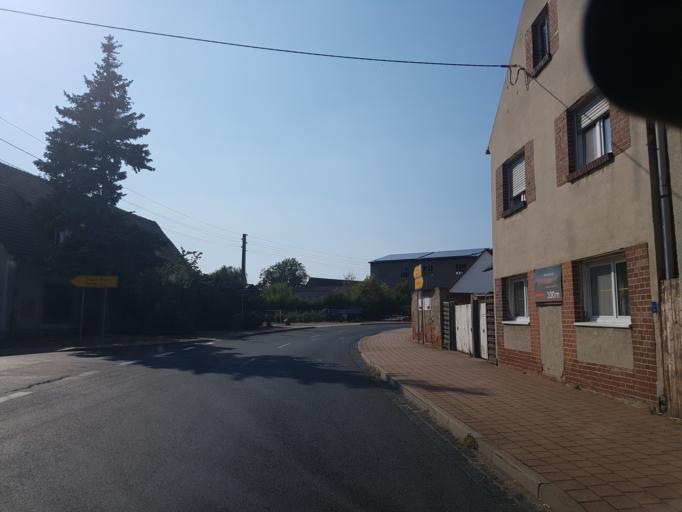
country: DE
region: Saxony-Anhalt
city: Annaburg
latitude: 51.6946
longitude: 12.9987
